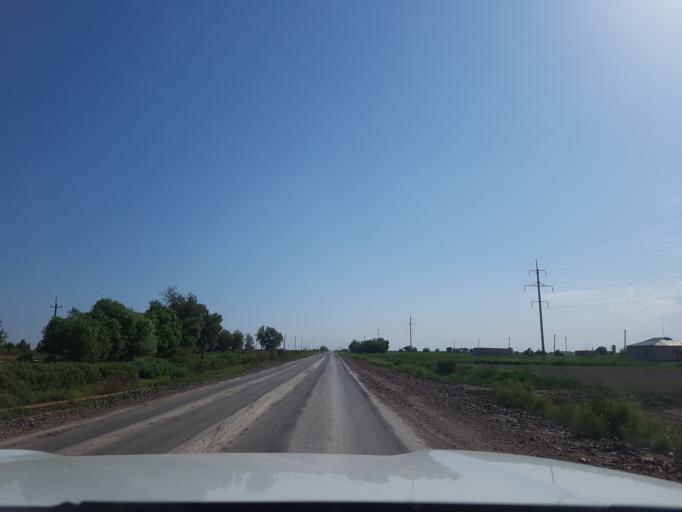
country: TM
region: Dasoguz
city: Koeneuergench
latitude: 42.0989
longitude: 58.9003
